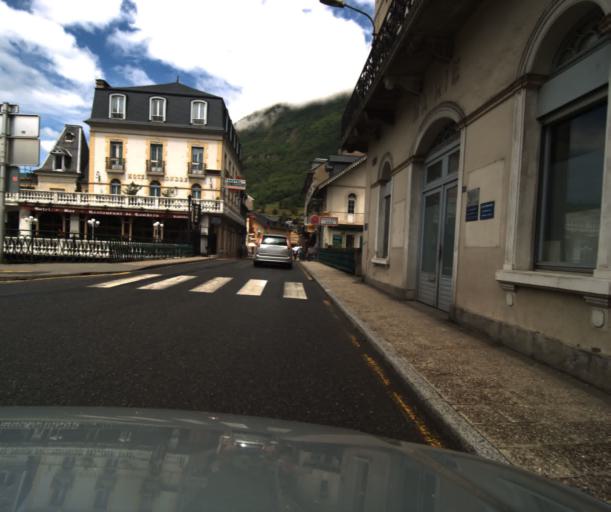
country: FR
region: Midi-Pyrenees
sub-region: Departement des Hautes-Pyrenees
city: Luz-Saint-Sauveur
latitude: 42.8736
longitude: -0.0032
